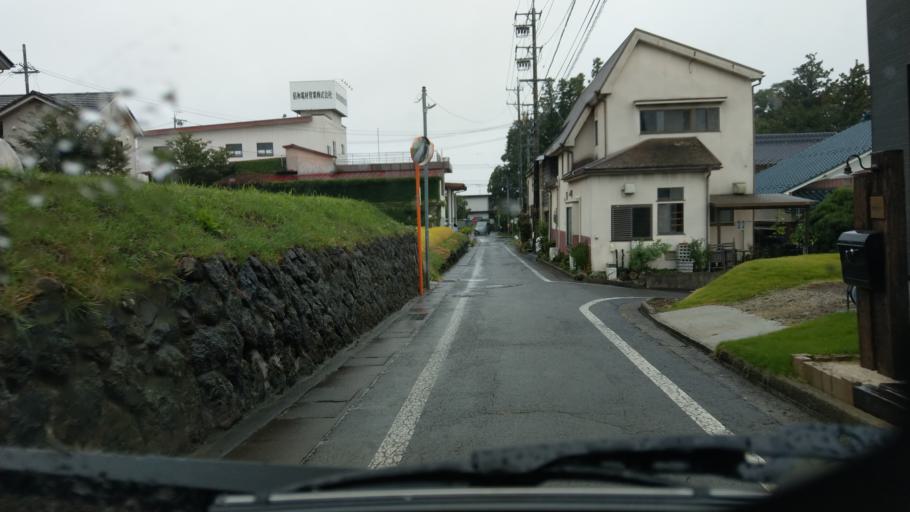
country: JP
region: Nagano
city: Komoro
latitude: 36.3271
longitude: 138.4320
